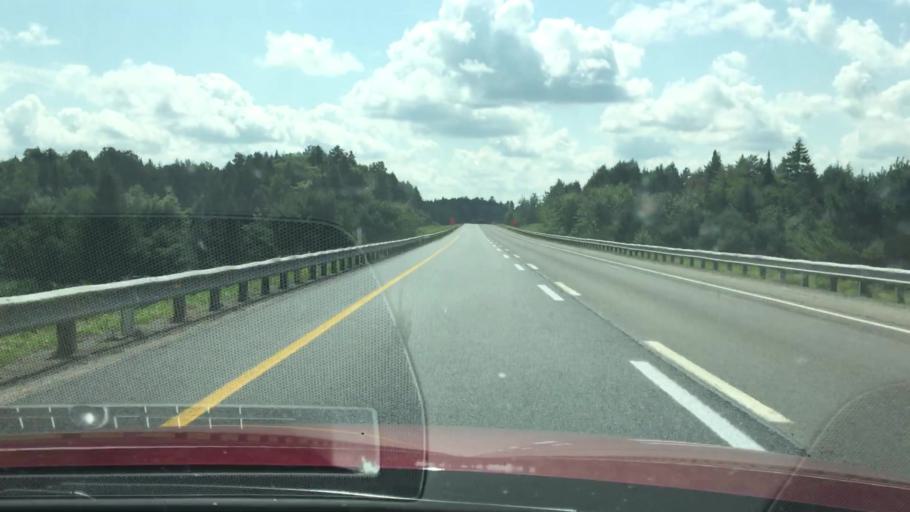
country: US
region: Maine
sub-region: Penobscot County
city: Medway
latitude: 45.6859
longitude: -68.4907
